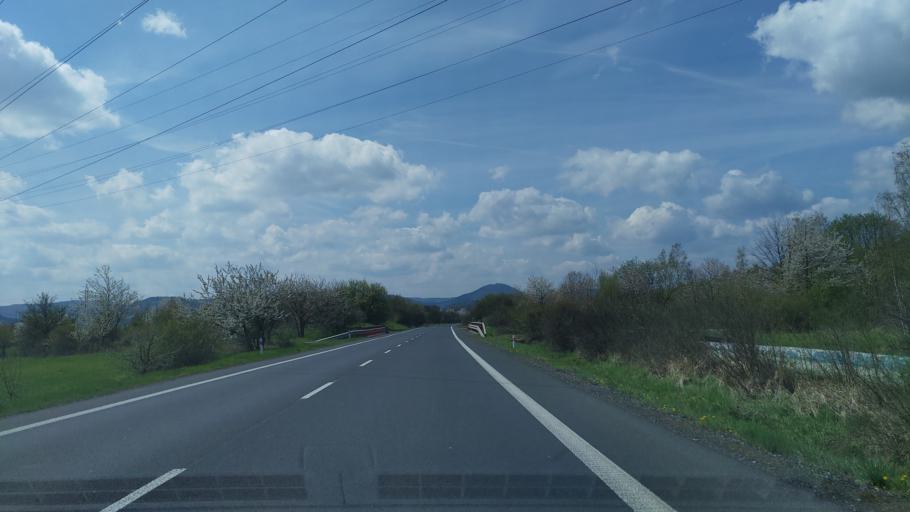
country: CZ
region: Ustecky
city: Kadan
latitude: 50.4100
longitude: 13.2440
